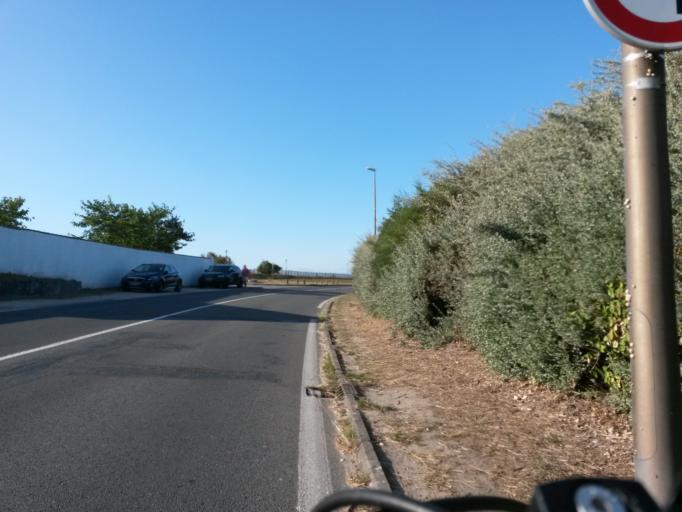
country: FR
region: Poitou-Charentes
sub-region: Departement de la Charente-Maritime
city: Rivedoux-Plage
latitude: 46.1580
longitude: -1.2653
